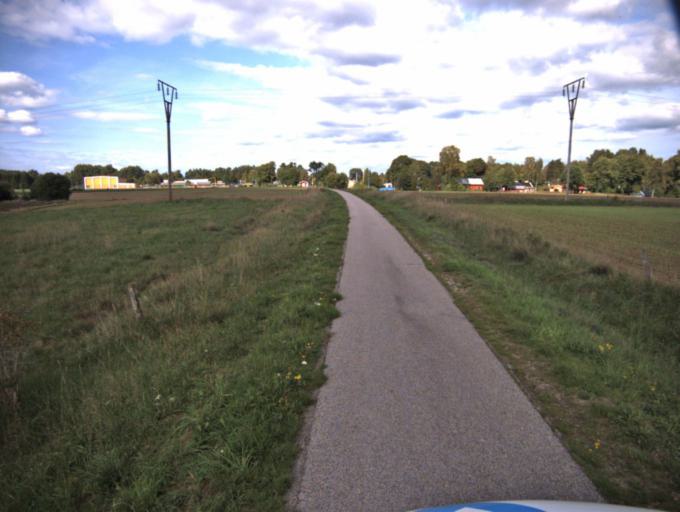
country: SE
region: Vaestra Goetaland
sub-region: Ulricehamns Kommun
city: Ulricehamn
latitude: 57.8529
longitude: 13.4273
